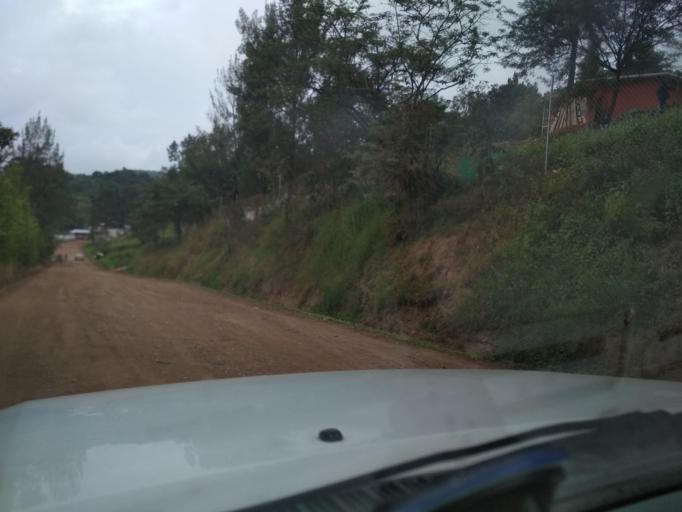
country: MX
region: Veracruz
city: El Castillo
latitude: 19.5399
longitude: -96.8313
